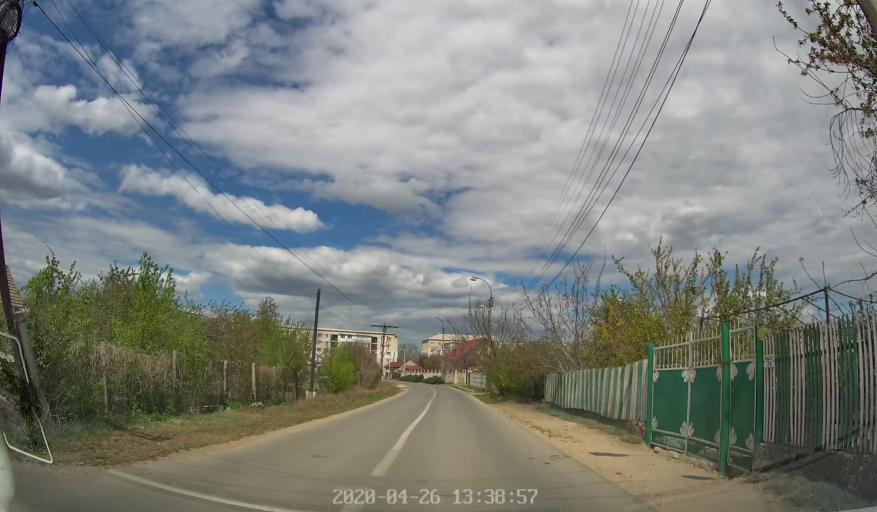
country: MD
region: Criuleni
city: Criuleni
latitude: 47.2114
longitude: 29.1650
